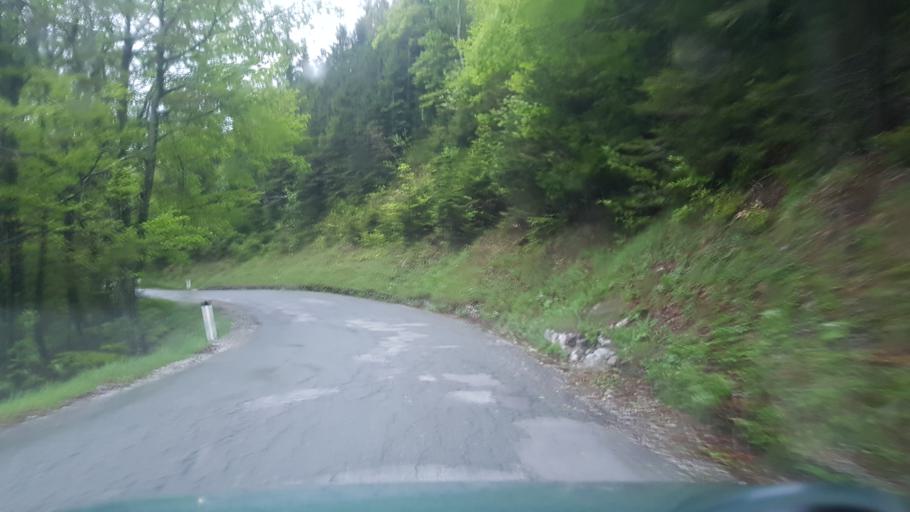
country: SI
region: Bohinj
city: Bohinjska Bistrica
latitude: 46.2304
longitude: 14.0227
